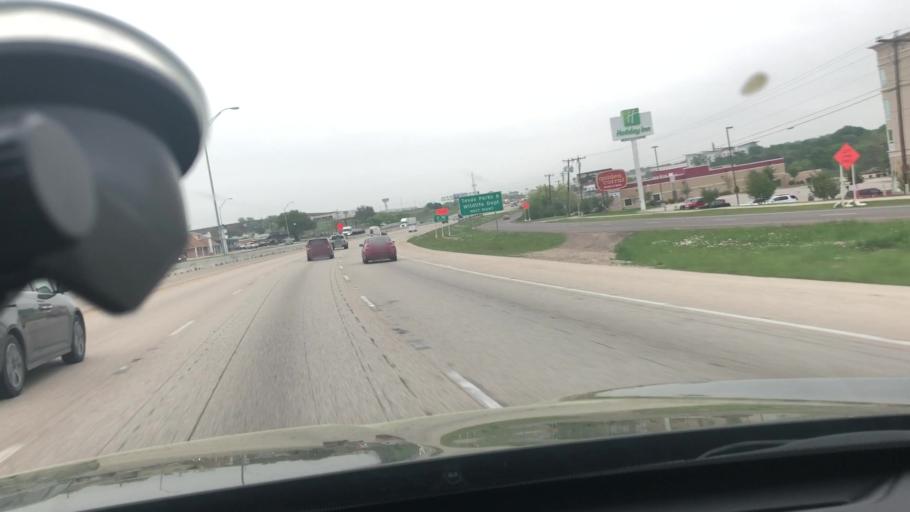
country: US
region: Texas
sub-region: Bell County
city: Belton
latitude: 31.0833
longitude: -97.4086
